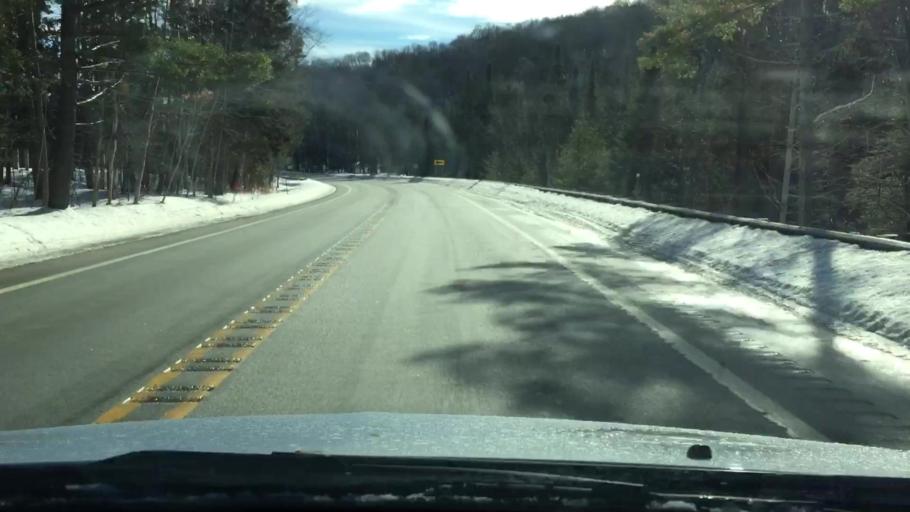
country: US
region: Michigan
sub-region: Antrim County
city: Mancelona
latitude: 45.0018
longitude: -85.0631
